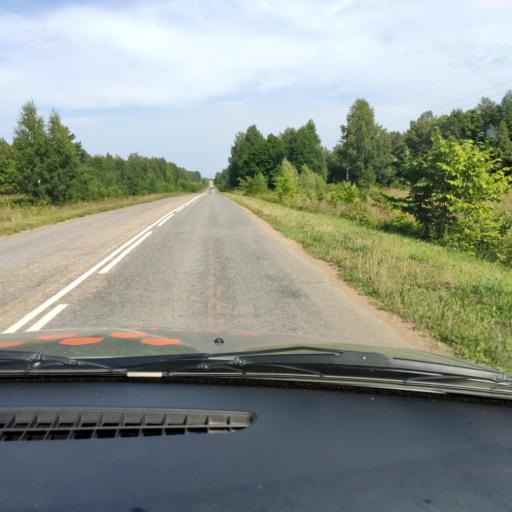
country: RU
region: Bashkortostan
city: Pavlovka
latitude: 55.3911
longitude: 56.5292
